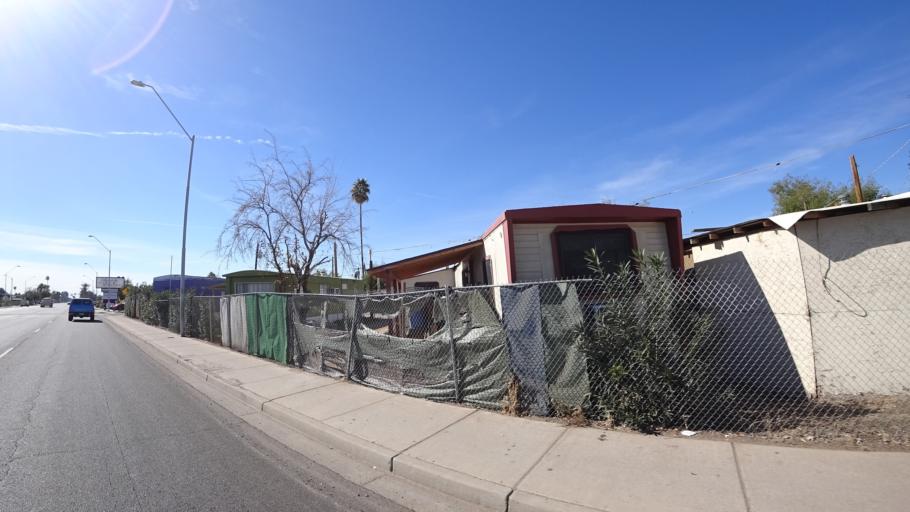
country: US
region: Arizona
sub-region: Maricopa County
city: Glendale
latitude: 33.5337
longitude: -112.1864
